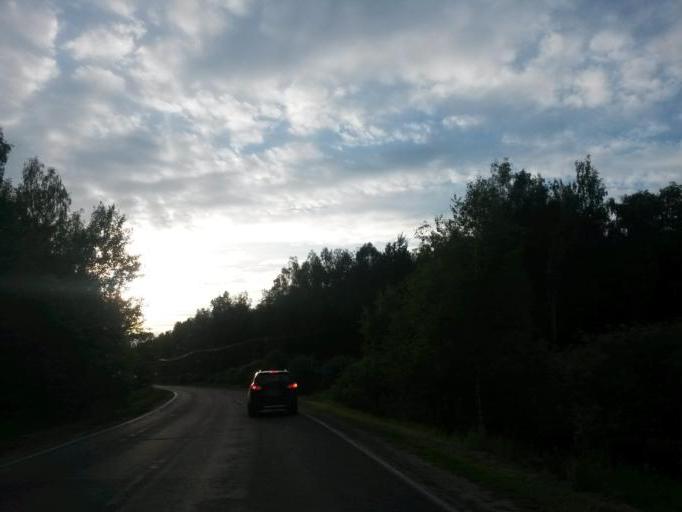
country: RU
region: Moskovskaya
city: Melikhovo
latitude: 55.2190
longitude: 37.6785
